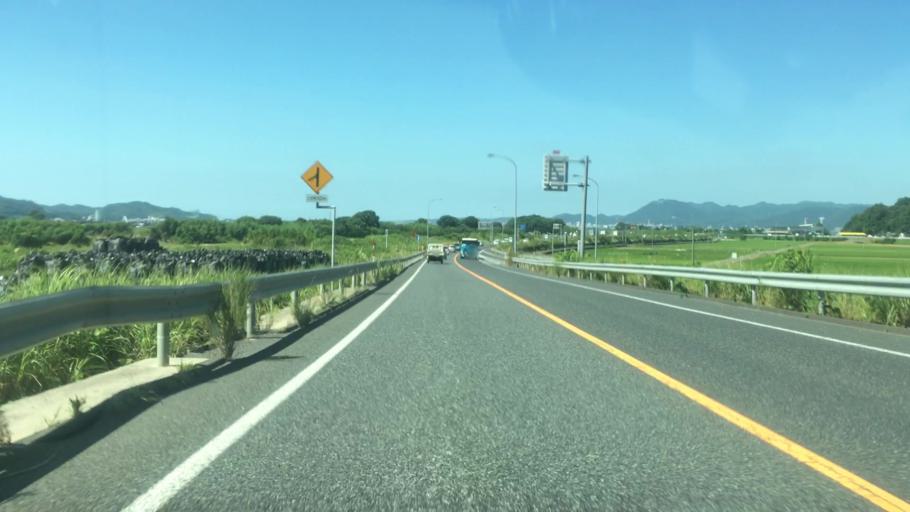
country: JP
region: Tottori
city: Tottori
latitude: 35.4418
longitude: 134.2100
